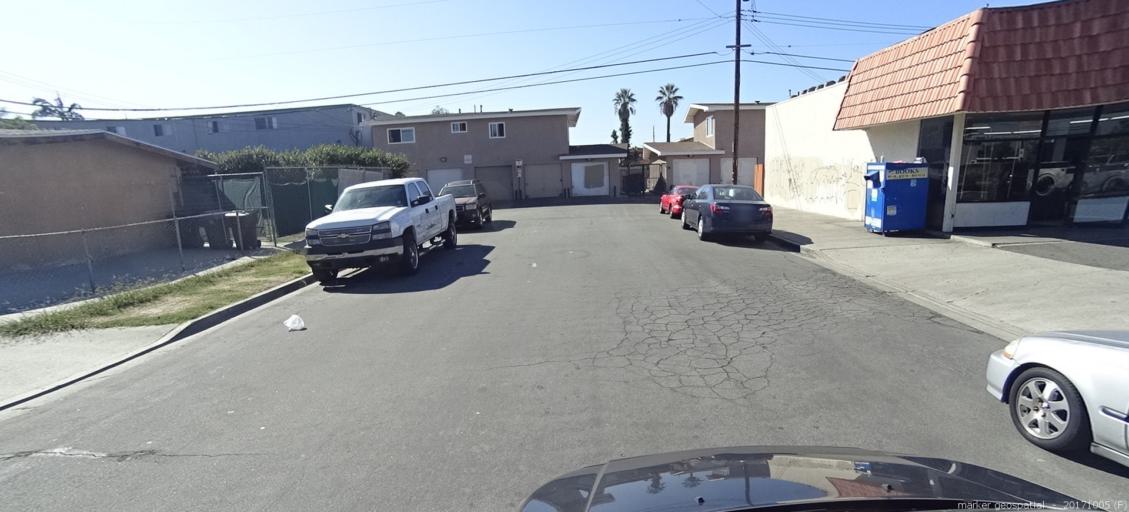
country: US
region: California
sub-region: Orange County
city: Stanton
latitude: 33.8028
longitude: -117.9661
